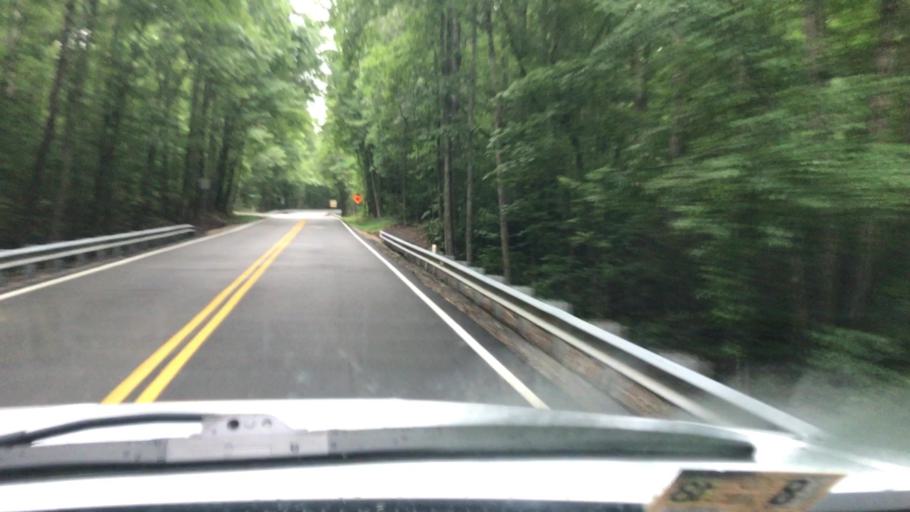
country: US
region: Virginia
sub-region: Henrico County
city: Short Pump
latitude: 37.6046
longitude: -77.6981
